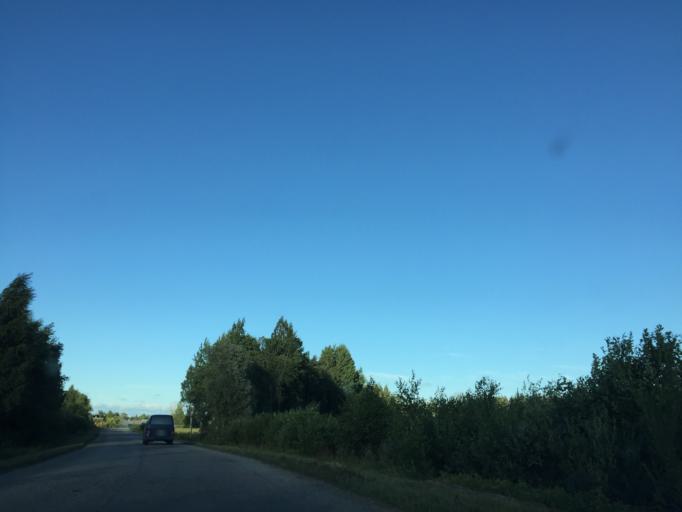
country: LV
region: Plavinu
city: Plavinas
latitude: 56.6091
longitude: 25.8290
